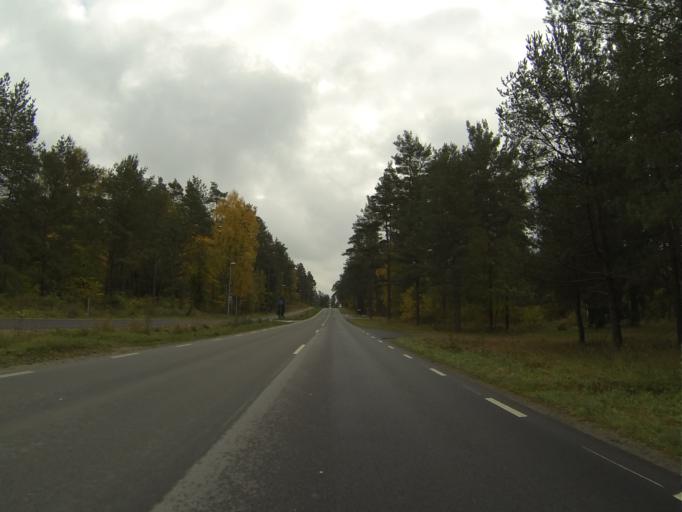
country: SE
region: Skane
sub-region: Sjobo Kommun
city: Sjoebo
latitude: 55.6346
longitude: 13.6556
